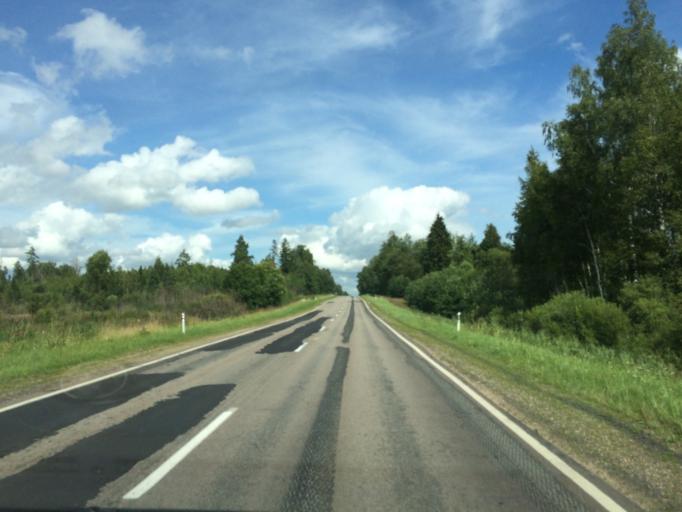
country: LV
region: Karsava
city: Karsava
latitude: 56.6509
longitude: 27.4970
